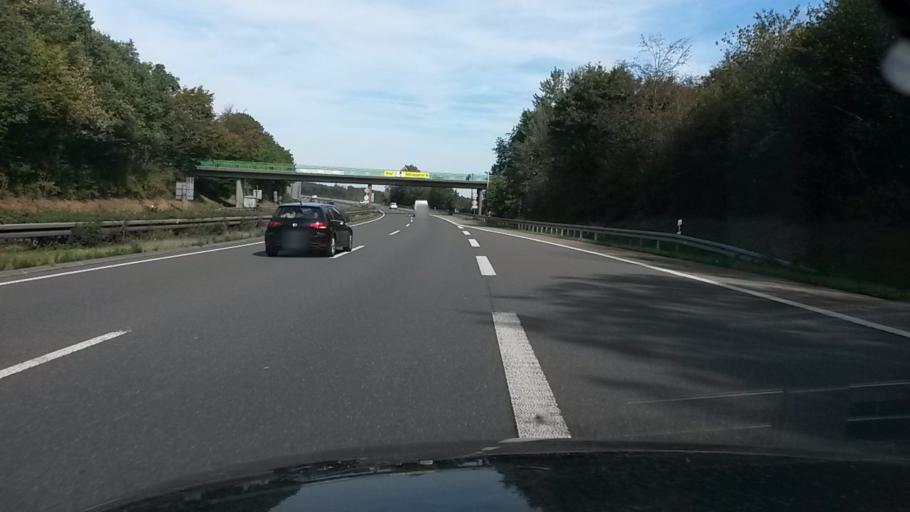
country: DE
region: North Rhine-Westphalia
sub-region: Regierungsbezirk Arnsberg
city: Luedenscheid
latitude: 51.1966
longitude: 7.6737
